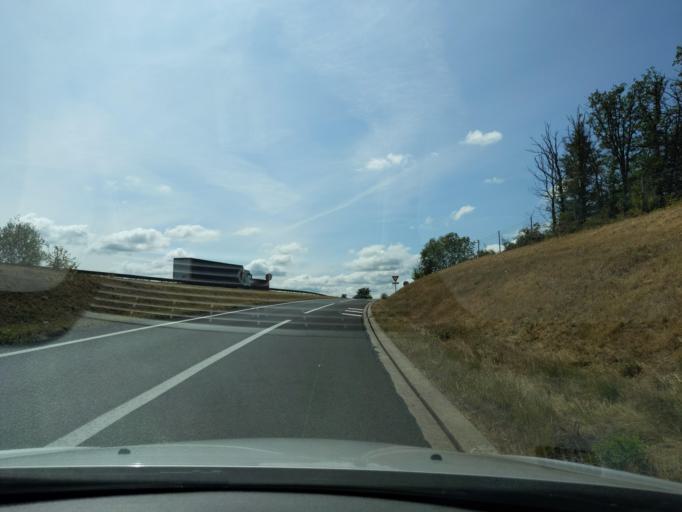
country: FR
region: Auvergne
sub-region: Departement de l'Allier
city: Desertines
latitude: 46.3869
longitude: 2.6954
